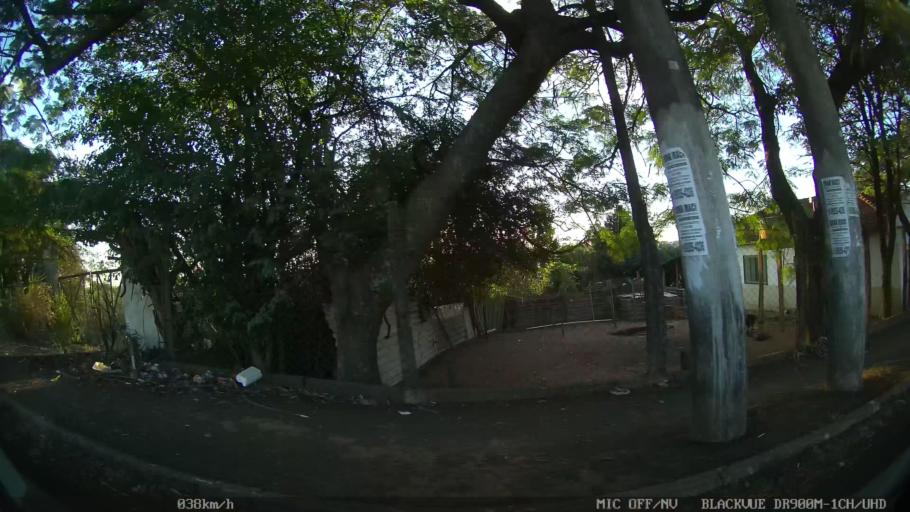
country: BR
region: Sao Paulo
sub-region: Franca
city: Franca
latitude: -20.5137
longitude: -47.4150
